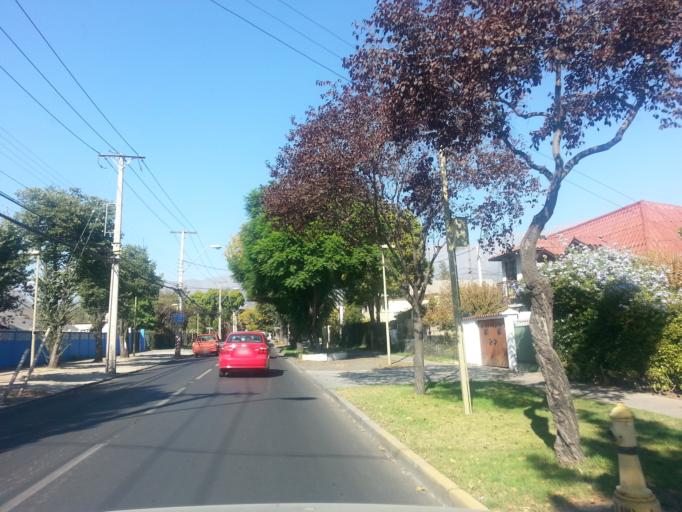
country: CL
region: Santiago Metropolitan
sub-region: Provincia de Santiago
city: Villa Presidente Frei, Nunoa, Santiago, Chile
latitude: -33.4259
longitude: -70.5701
